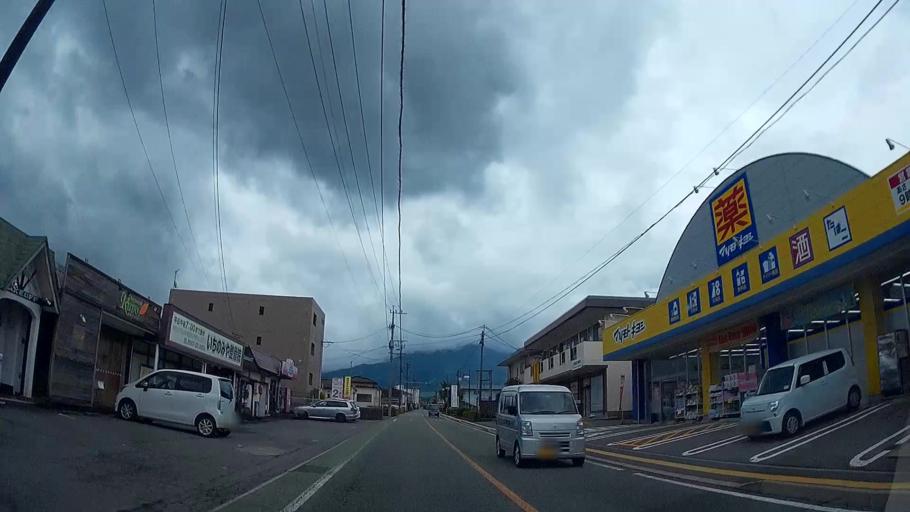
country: JP
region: Kumamoto
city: Aso
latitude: 32.9446
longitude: 131.1178
